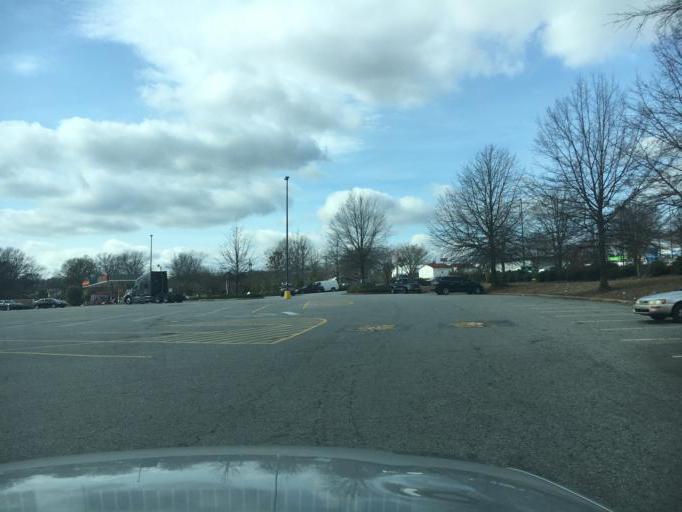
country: US
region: South Carolina
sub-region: Greenville County
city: Greer
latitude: 34.9461
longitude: -82.2061
